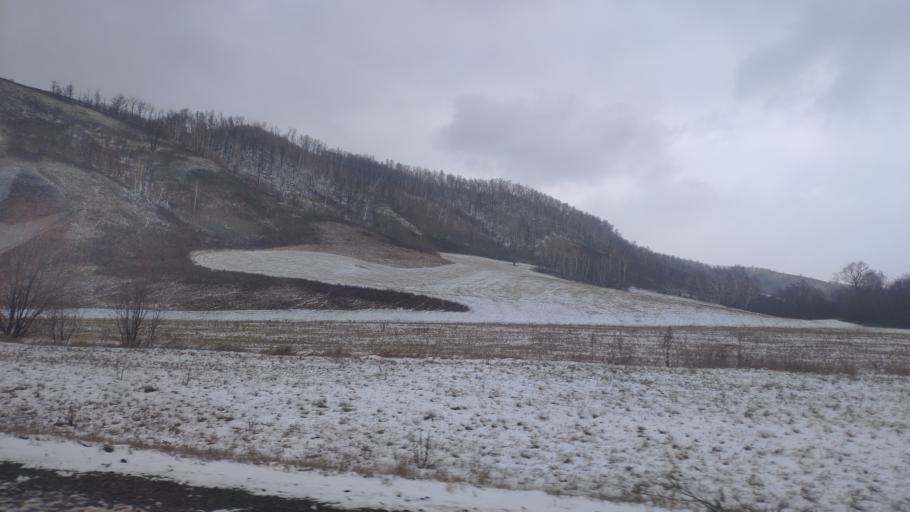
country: RU
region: Bashkortostan
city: Isyangulovo
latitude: 52.1607
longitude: 56.9223
